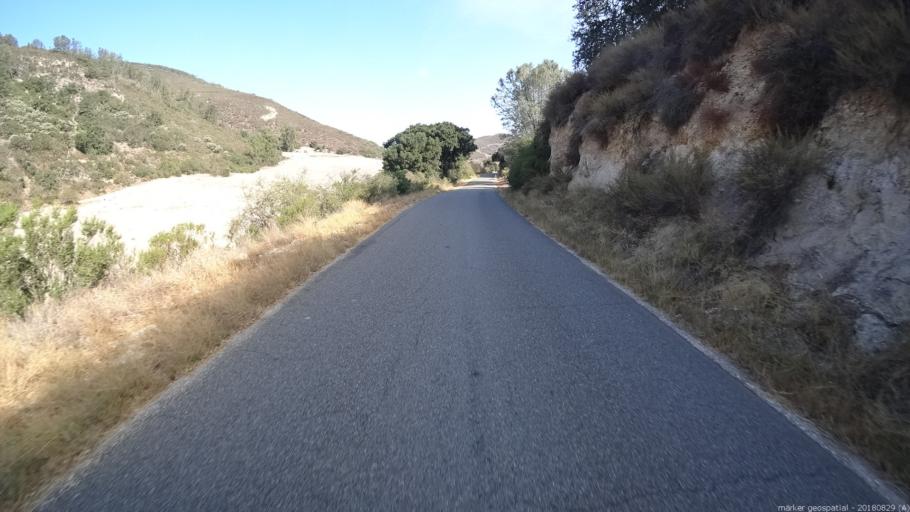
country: US
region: California
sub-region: Monterey County
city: King City
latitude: 36.0315
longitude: -121.0762
